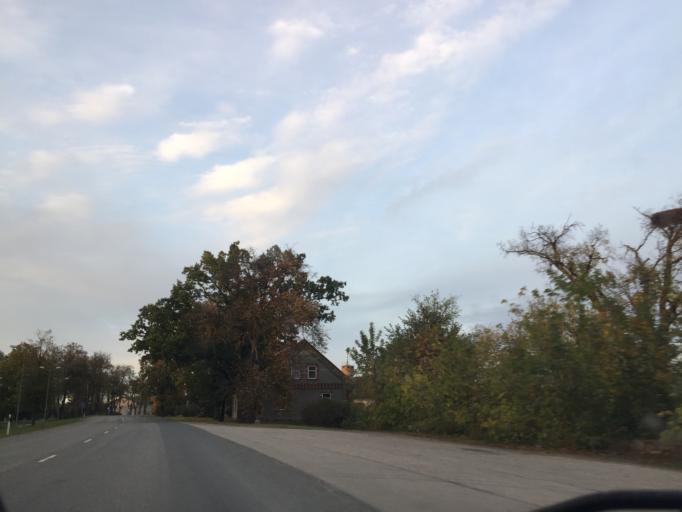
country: LV
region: Dobeles Rajons
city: Dobele
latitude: 56.7359
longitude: 23.3919
